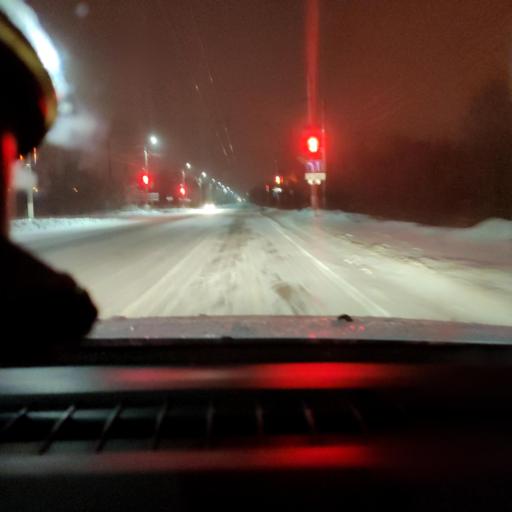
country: RU
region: Samara
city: Novokuybyshevsk
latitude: 53.0793
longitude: 49.9298
